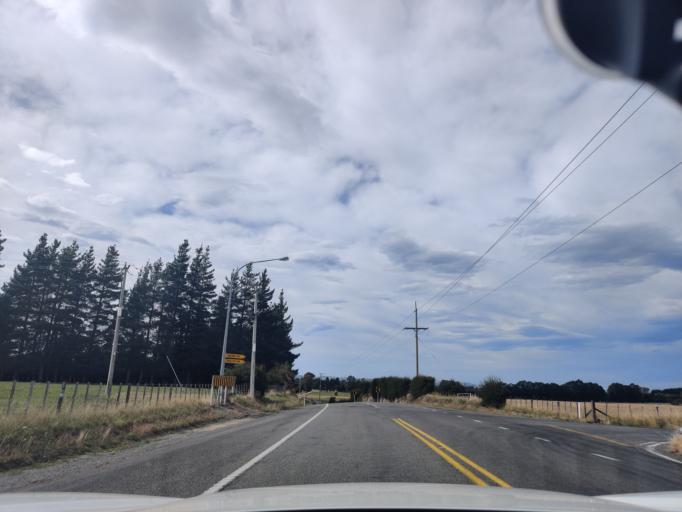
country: NZ
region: Wellington
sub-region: Masterton District
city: Masterton
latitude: -40.8425
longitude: 175.6315
